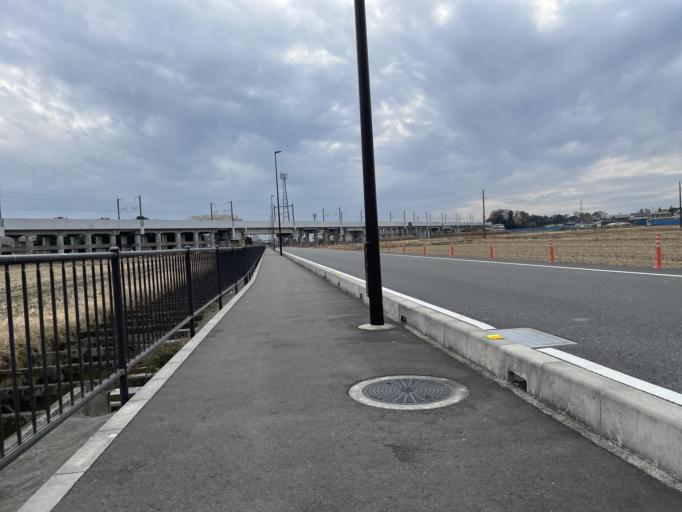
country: JP
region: Saitama
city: Shiraoka
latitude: 36.0132
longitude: 139.6473
